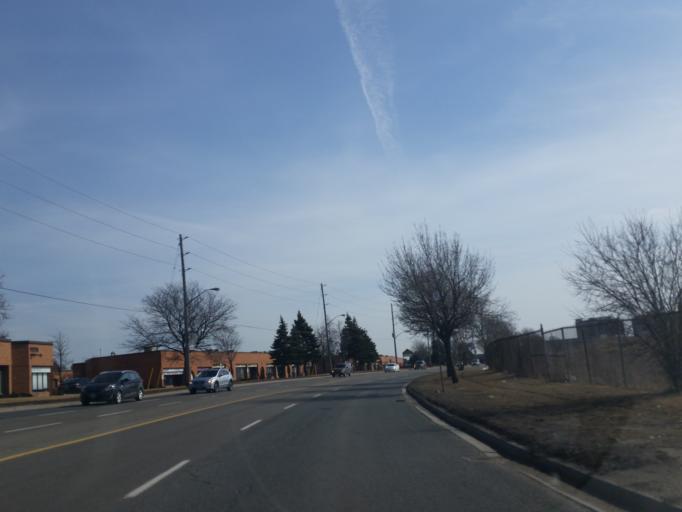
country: CA
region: Ontario
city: Concord
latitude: 43.7554
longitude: -79.4736
